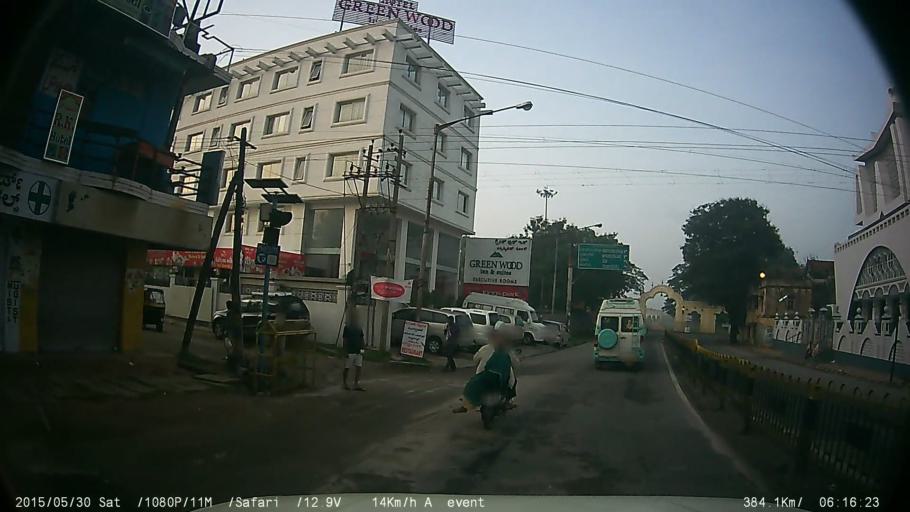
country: IN
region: Karnataka
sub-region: Mysore
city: Mysore
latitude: 12.3196
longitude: 76.6618
